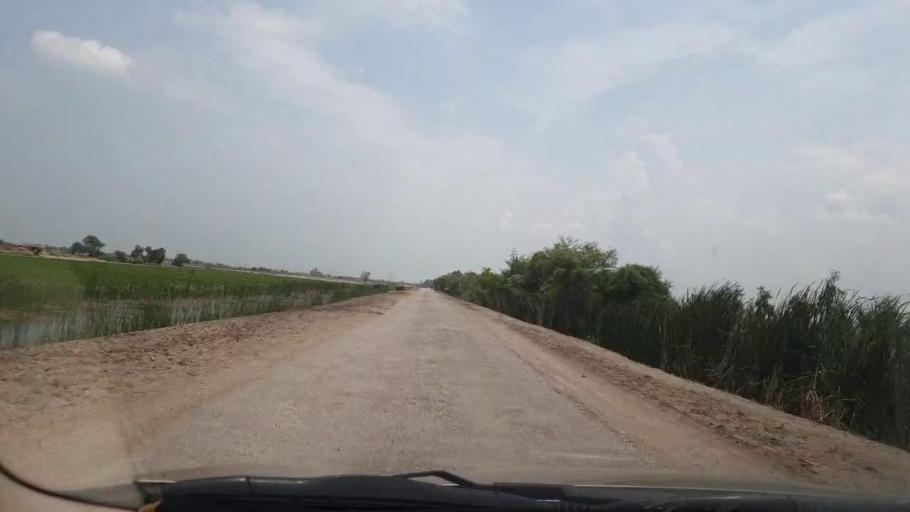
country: PK
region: Sindh
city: Larkana
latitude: 27.6074
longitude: 68.1648
